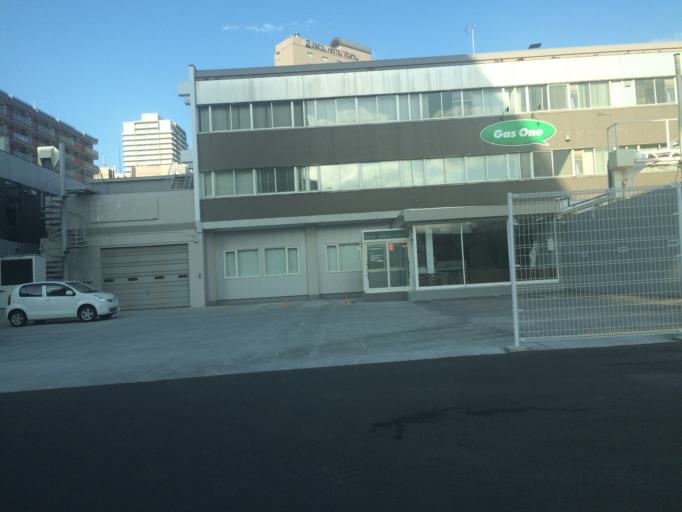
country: JP
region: Hokkaido
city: Sapporo
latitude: 43.0493
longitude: 141.3497
